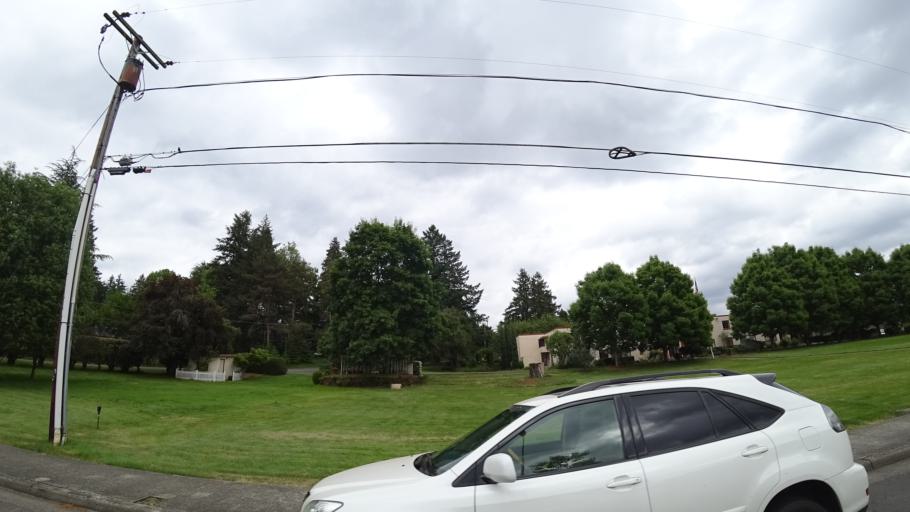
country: US
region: Oregon
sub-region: Washington County
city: West Slope
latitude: 45.4955
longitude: -122.7825
